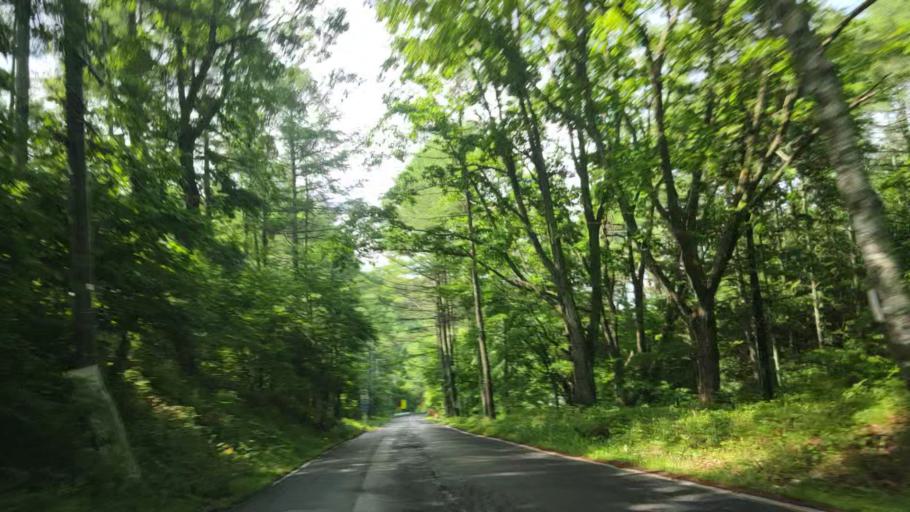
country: JP
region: Nagano
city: Suwa
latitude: 36.0866
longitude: 138.1437
